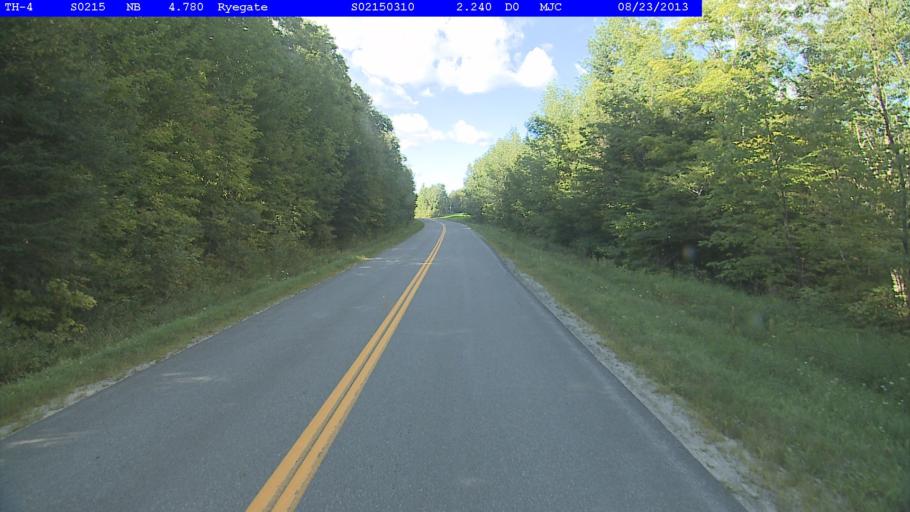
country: US
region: New Hampshire
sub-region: Grafton County
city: Woodsville
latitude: 44.2732
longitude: -72.1737
